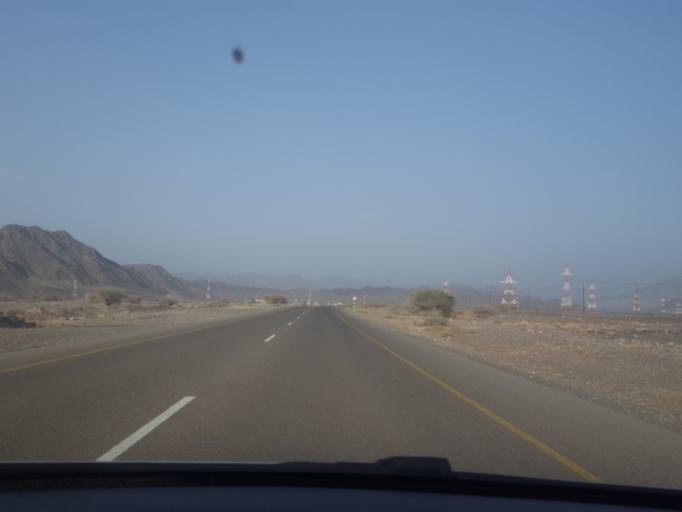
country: AE
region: Abu Dhabi
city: Al Ain
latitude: 24.0485
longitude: 56.0514
